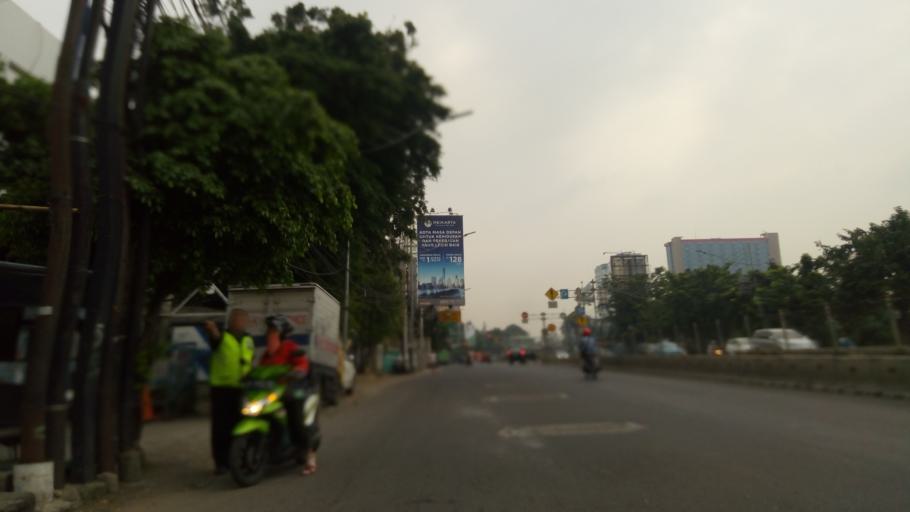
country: ID
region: Jakarta Raya
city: Jakarta
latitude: -6.1437
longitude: 106.8341
